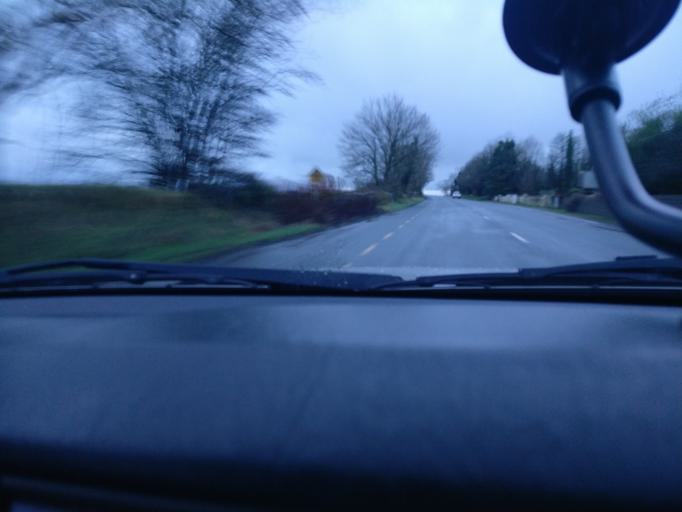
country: IE
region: Connaught
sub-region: County Galway
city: Loughrea
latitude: 53.2652
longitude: -8.4177
